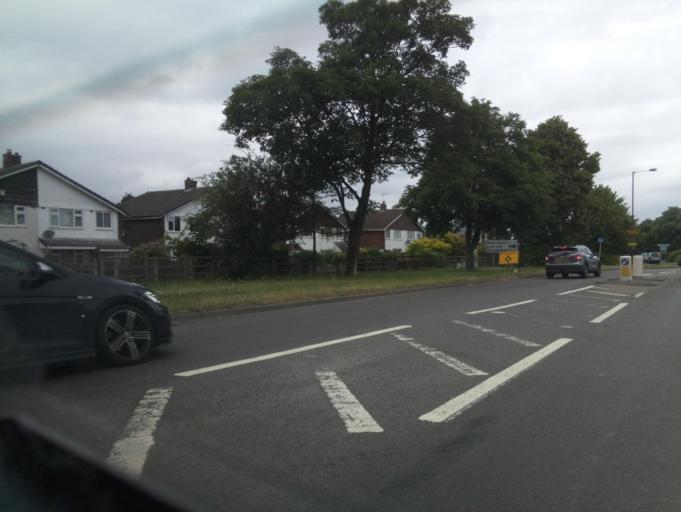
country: GB
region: England
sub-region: Staffordshire
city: Penkridge
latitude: 52.7174
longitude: -2.1188
